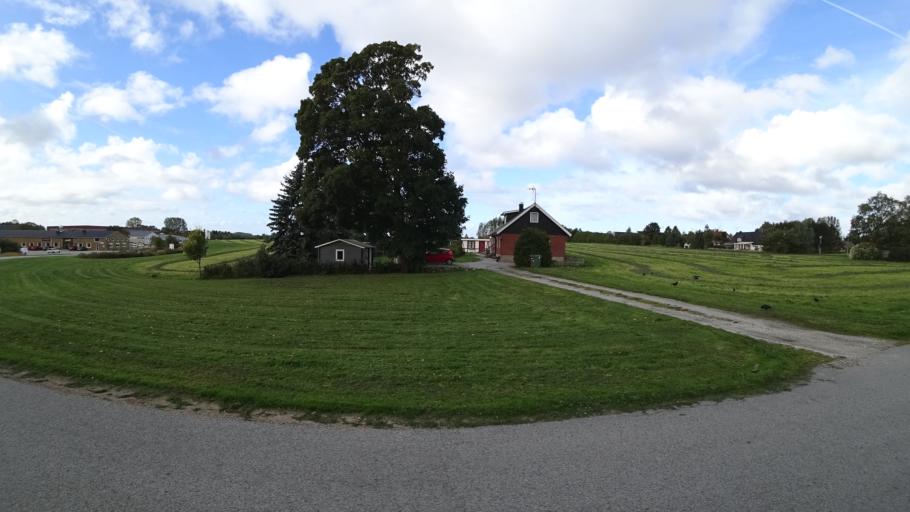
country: SE
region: Skane
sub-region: Kavlinge Kommun
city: Loddekopinge
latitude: 55.7668
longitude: 13.0539
